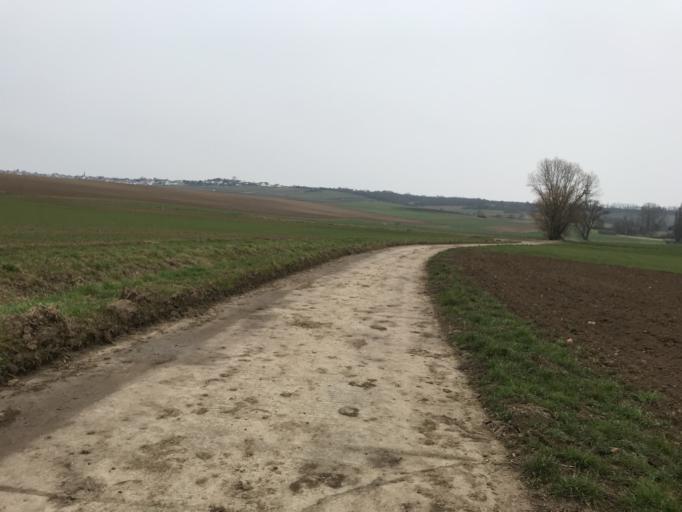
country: DE
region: Rheinland-Pfalz
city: Ober-Olm
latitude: 49.9270
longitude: 8.1828
